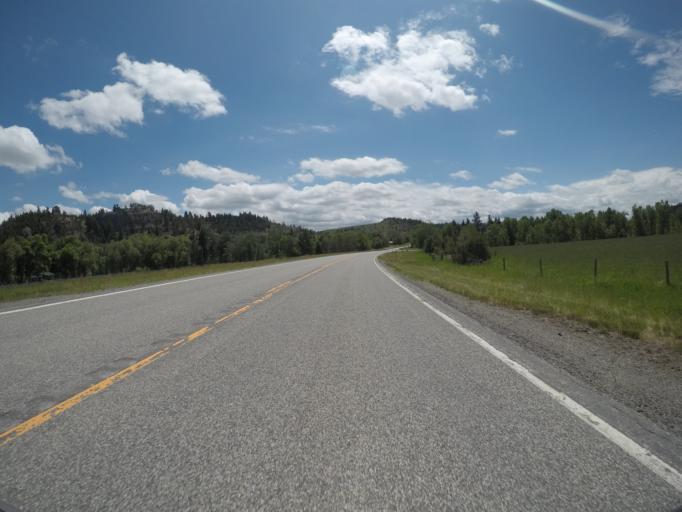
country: US
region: Montana
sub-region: Sweet Grass County
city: Big Timber
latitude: 45.7250
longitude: -109.9969
